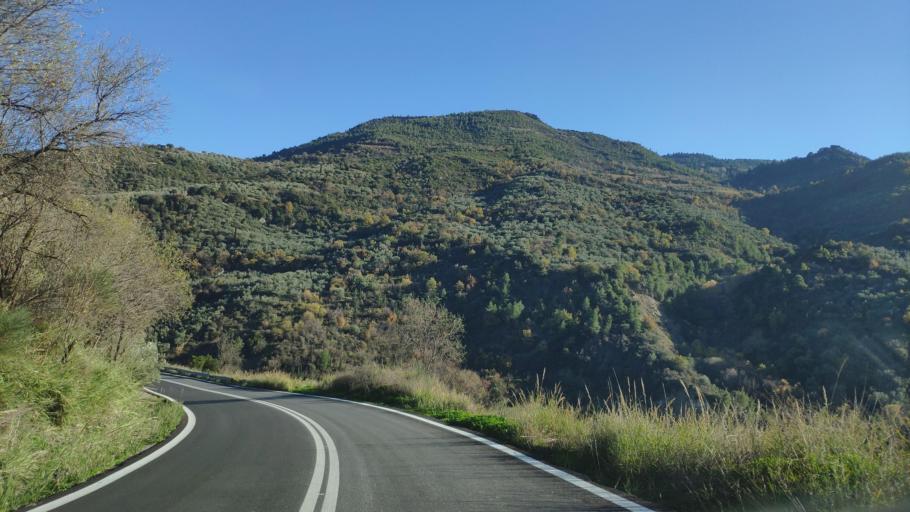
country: GR
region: Peloponnese
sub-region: Nomos Korinthias
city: Xylokastro
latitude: 38.0009
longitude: 22.5042
